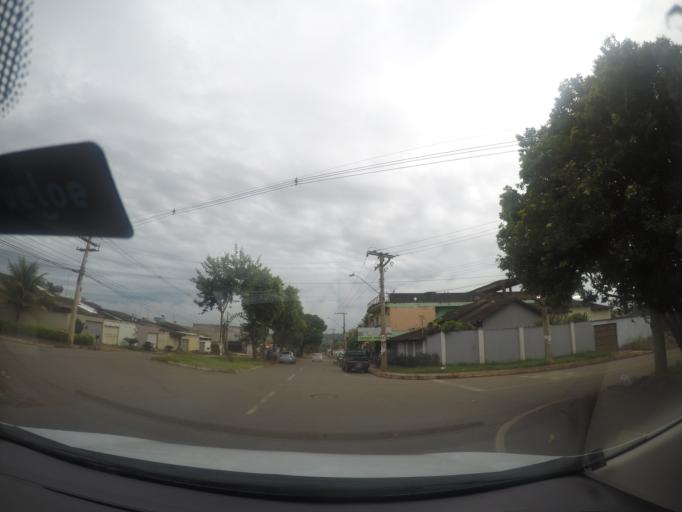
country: BR
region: Goias
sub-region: Goiania
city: Goiania
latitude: -16.5997
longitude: -49.3055
